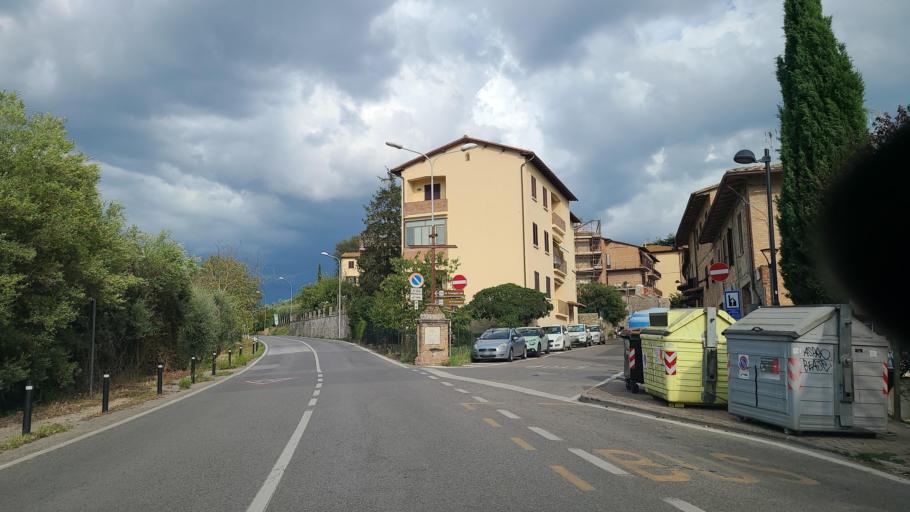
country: IT
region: Tuscany
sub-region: Provincia di Siena
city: San Gimignano
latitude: 43.4712
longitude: 11.0380
